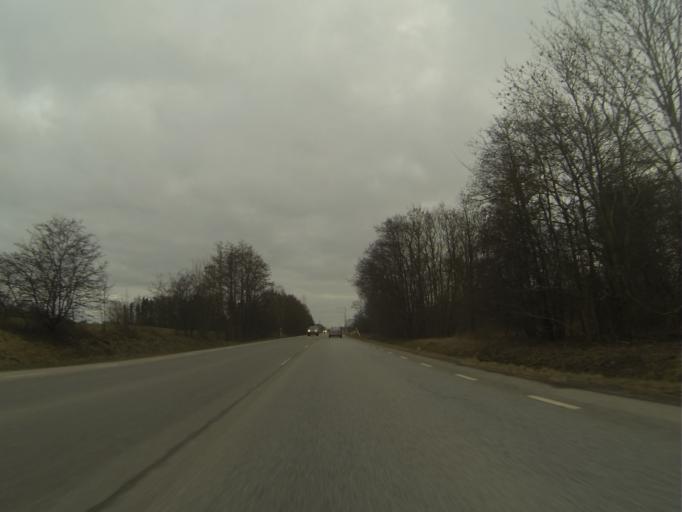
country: SE
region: Skane
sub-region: Svedala Kommun
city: Svedala
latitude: 55.5215
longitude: 13.2067
